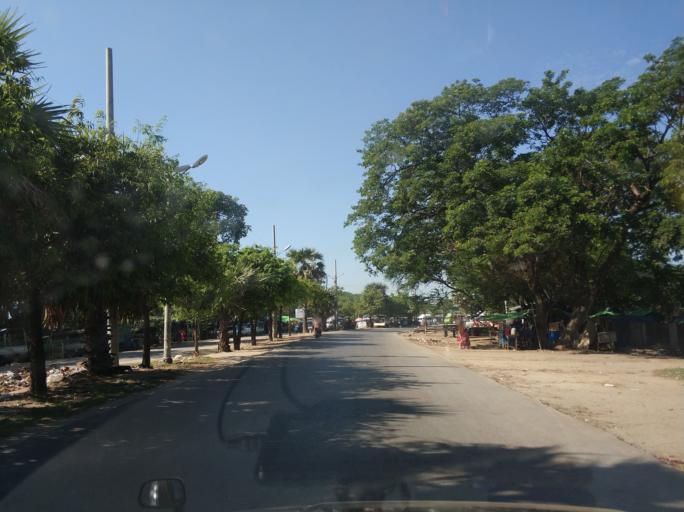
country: MM
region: Mandalay
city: Mandalay
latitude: 21.9627
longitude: 96.0558
